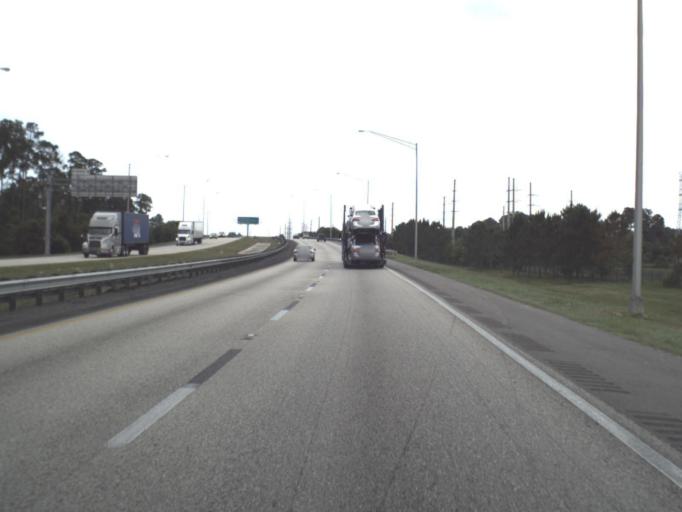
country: US
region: Florida
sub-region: Duval County
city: Neptune Beach
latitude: 30.3046
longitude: -81.5238
